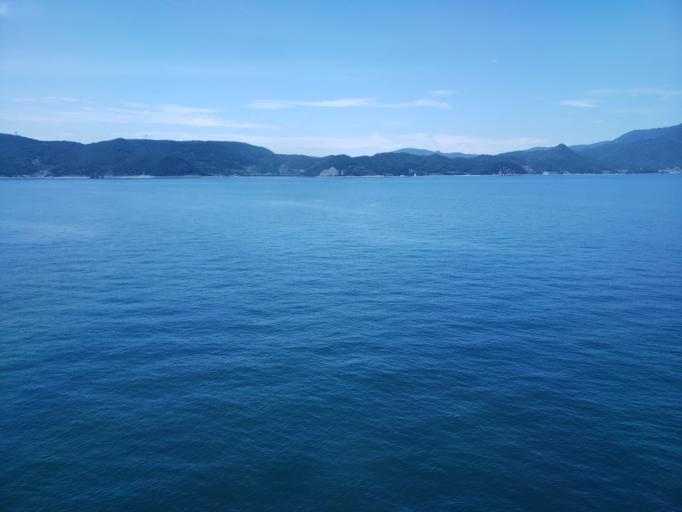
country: JP
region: Kagawa
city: Tonosho
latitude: 34.4241
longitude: 134.2724
